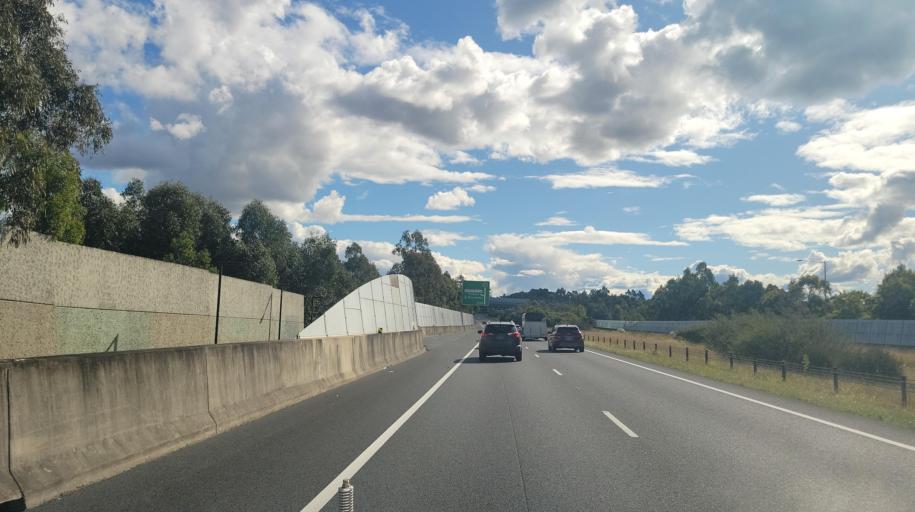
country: AU
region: New South Wales
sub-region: Blacktown
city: Blacktown
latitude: -33.7482
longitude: 150.9446
